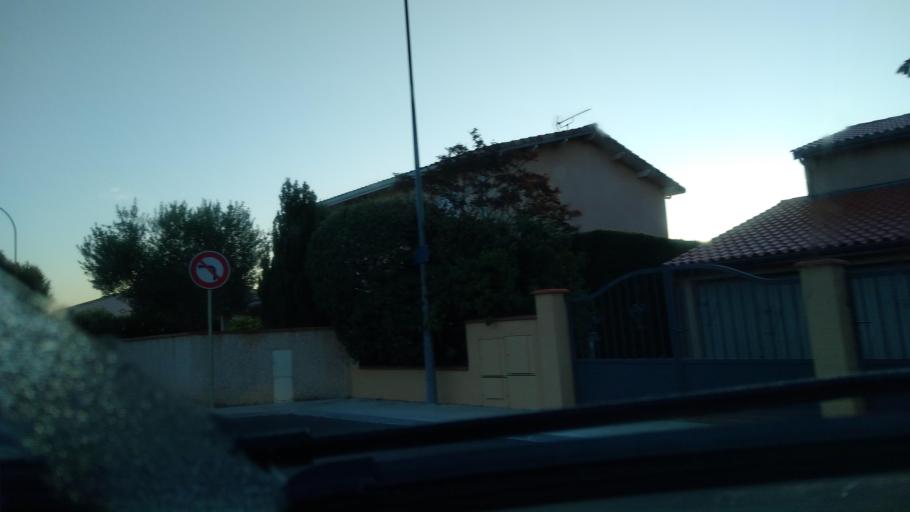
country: FR
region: Midi-Pyrenees
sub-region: Departement de la Haute-Garonne
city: Pibrac
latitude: 43.6132
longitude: 1.2890
